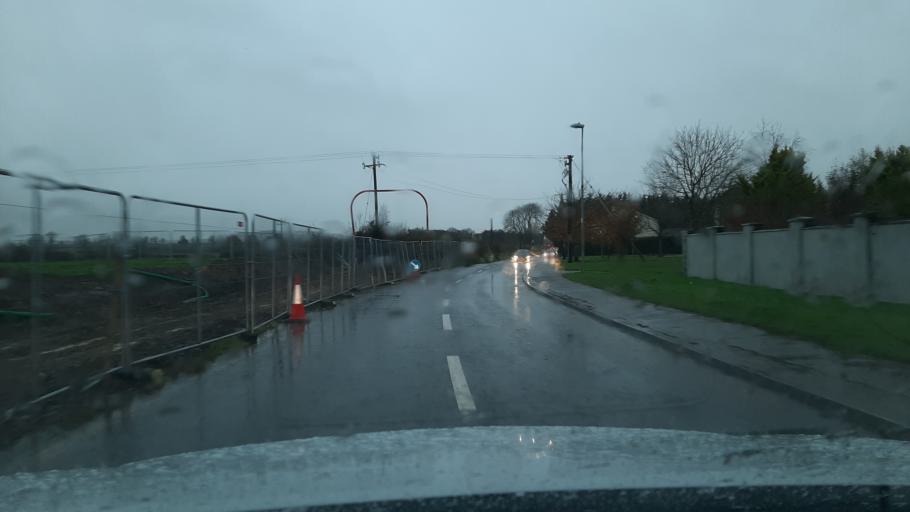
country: IE
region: Leinster
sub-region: Kildare
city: Kildare
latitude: 53.1651
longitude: -6.9130
